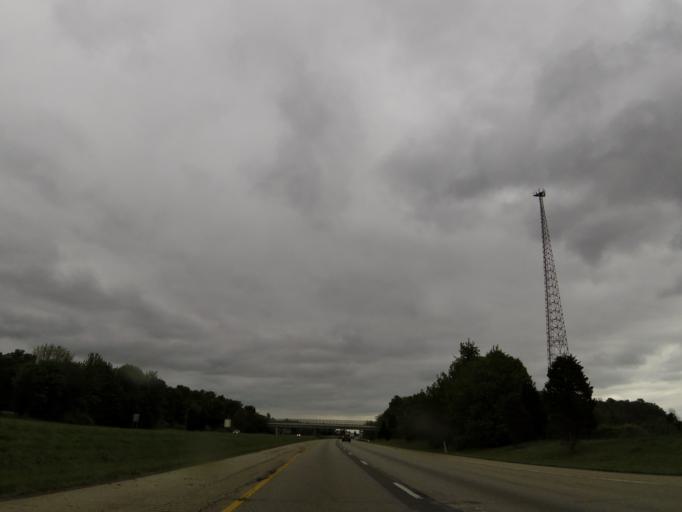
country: US
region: Ohio
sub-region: Warren County
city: Morrow
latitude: 39.4331
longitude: -84.0741
